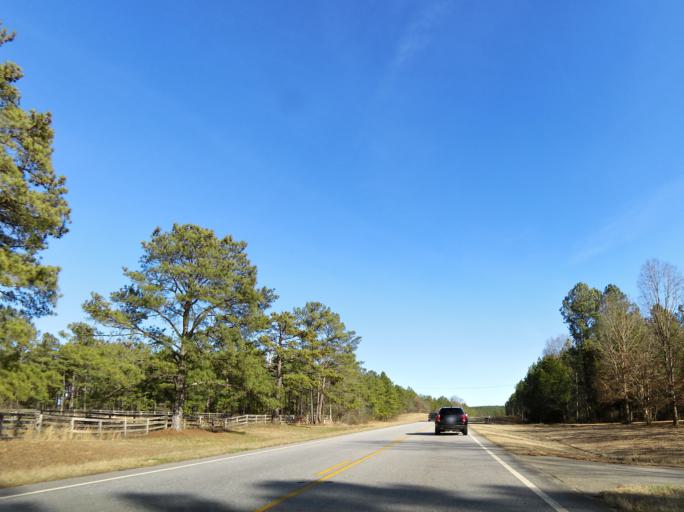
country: US
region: Georgia
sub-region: Crawford County
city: Roberta
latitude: 32.7516
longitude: -84.0898
